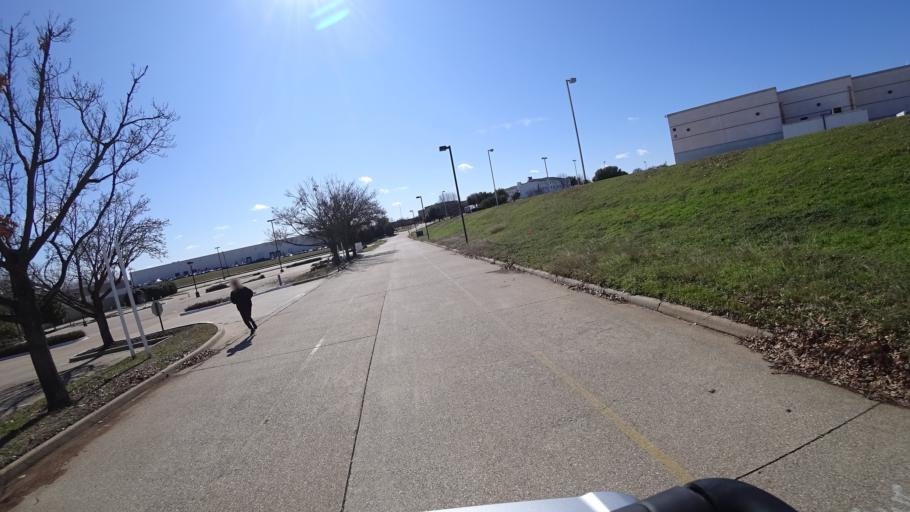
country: US
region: Texas
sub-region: Denton County
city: Lewisville
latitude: 33.0234
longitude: -96.9826
